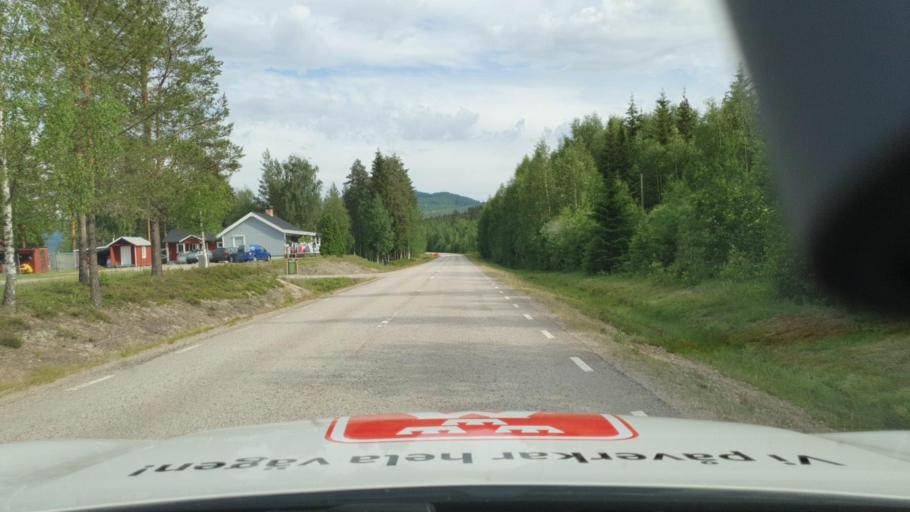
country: NO
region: Hedmark
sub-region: Trysil
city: Innbygda
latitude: 60.9074
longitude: 12.5616
